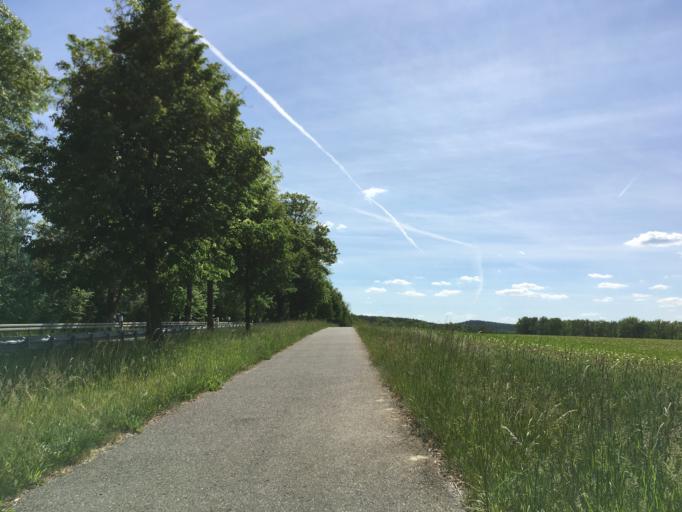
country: DE
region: Brandenburg
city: Oderberg
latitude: 52.8289
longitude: 14.0726
